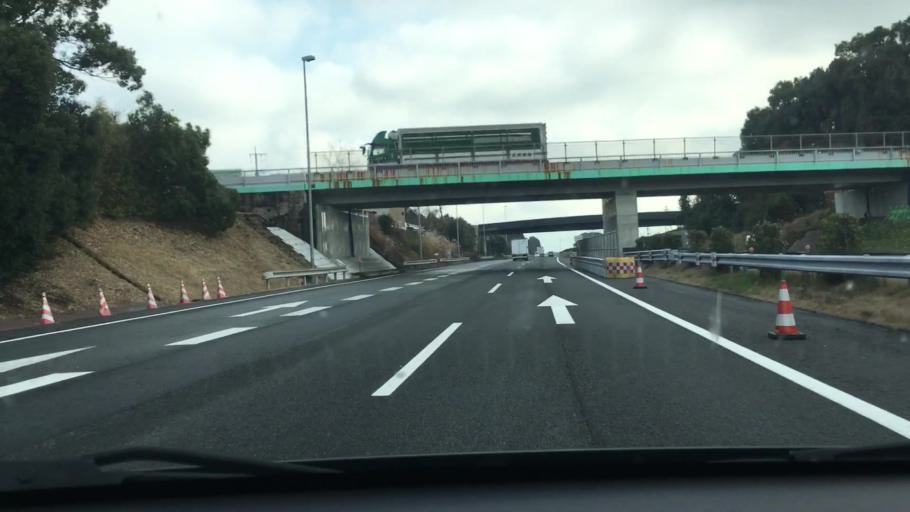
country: JP
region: Kumamoto
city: Kumamoto
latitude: 32.8348
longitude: 130.7794
